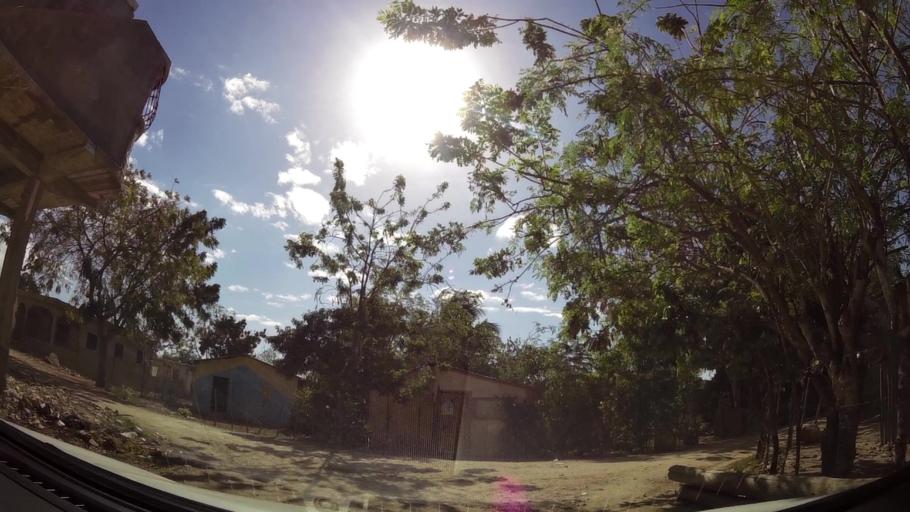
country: DO
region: Santo Domingo
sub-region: Santo Domingo
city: Boca Chica
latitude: 18.4636
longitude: -69.6013
